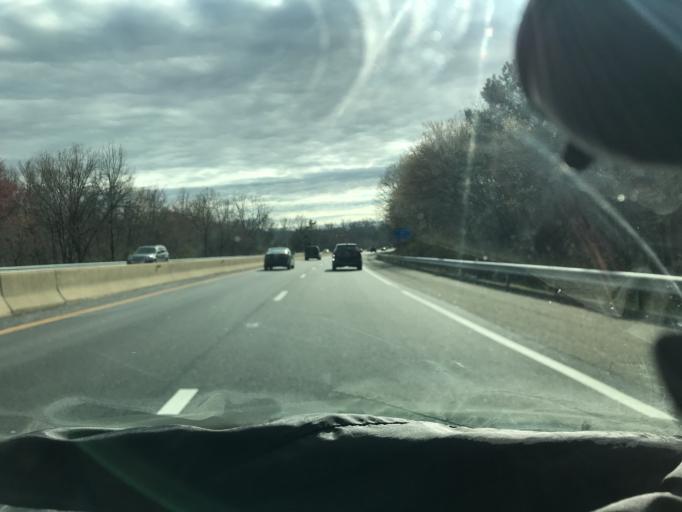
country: US
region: Virginia
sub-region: Chesterfield County
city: Bon Air
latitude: 37.5127
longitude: -77.5376
